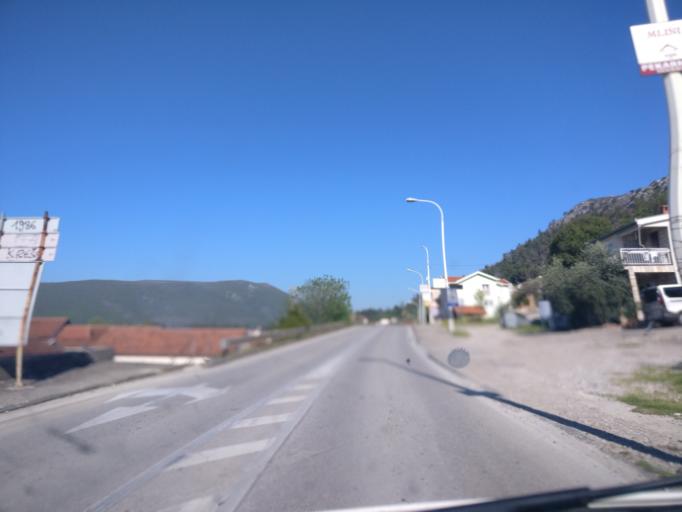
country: BA
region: Federation of Bosnia and Herzegovina
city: Capljina
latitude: 43.1153
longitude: 17.7015
